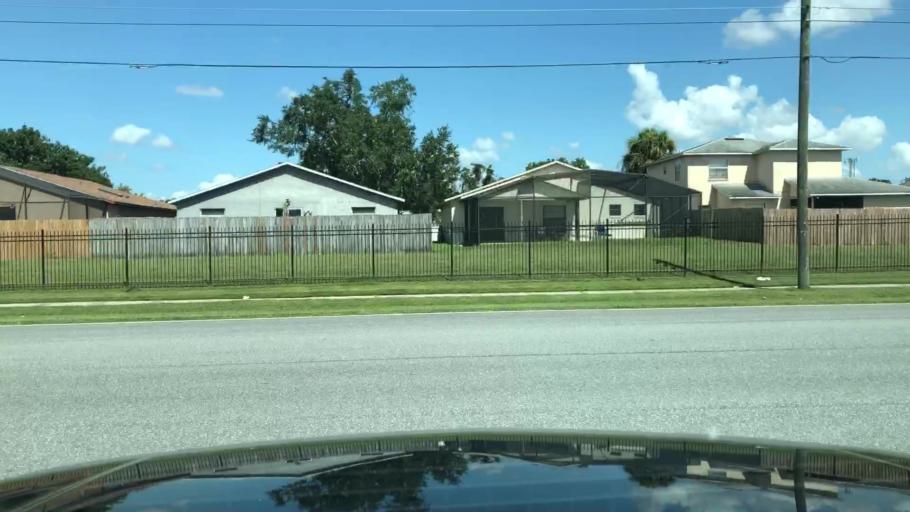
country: US
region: Florida
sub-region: Osceola County
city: Celebration
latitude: 28.3184
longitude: -81.4767
